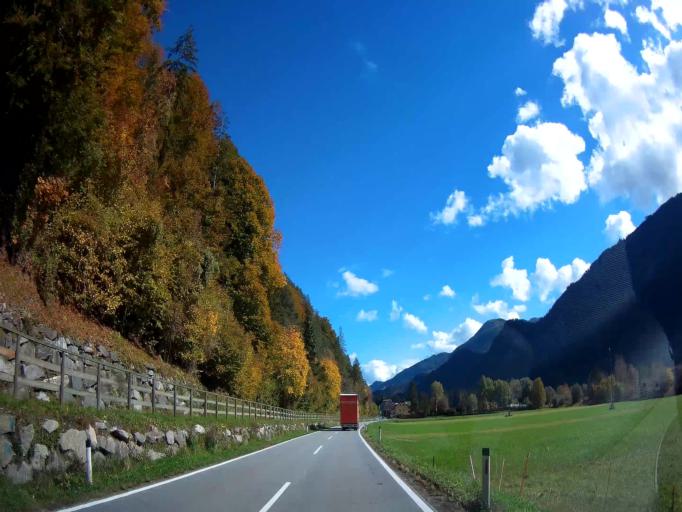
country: AT
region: Carinthia
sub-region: Politischer Bezirk Spittal an der Drau
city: Dellach im Drautal
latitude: 46.7379
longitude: 13.0730
